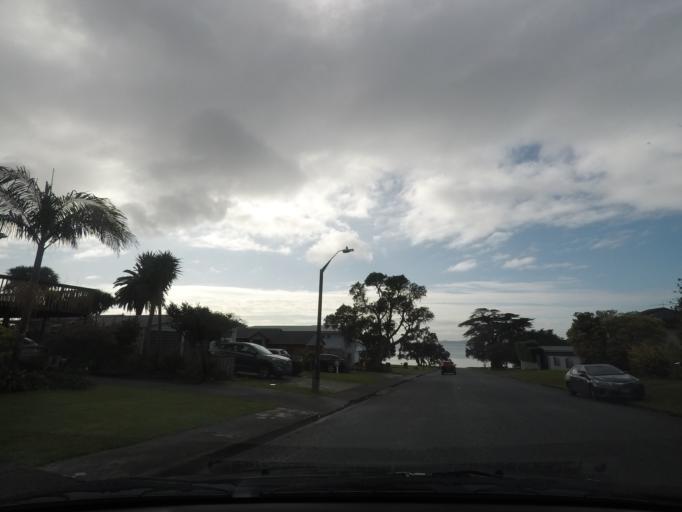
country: NZ
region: Auckland
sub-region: Auckland
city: Warkworth
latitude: -36.4198
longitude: 174.7283
